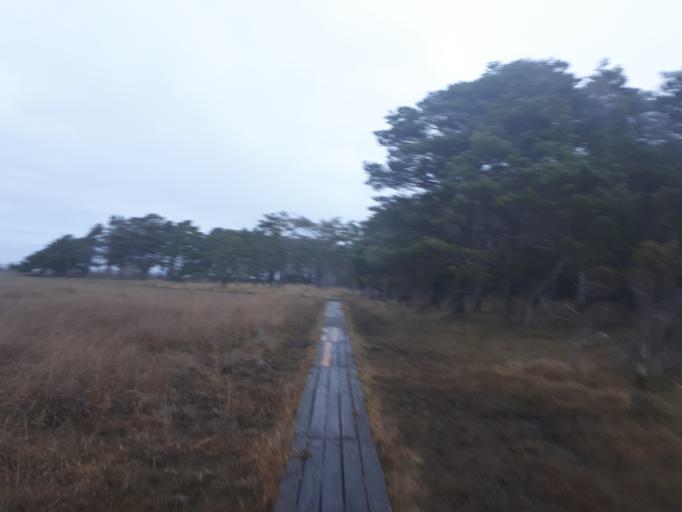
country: SE
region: Gotland
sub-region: Gotland
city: Visby
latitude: 57.6862
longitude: 18.3465
